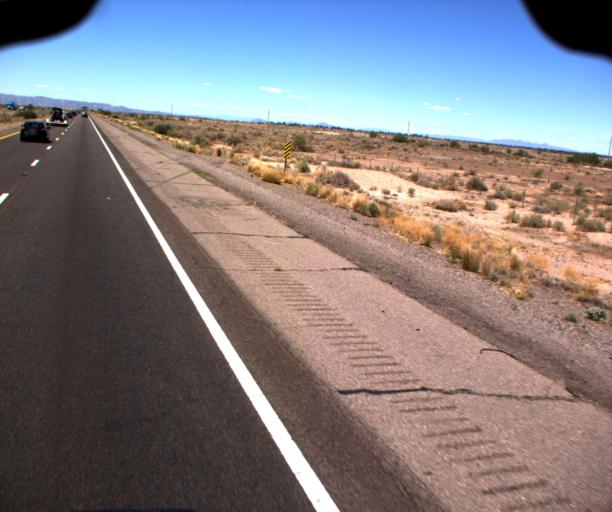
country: US
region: Arizona
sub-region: Pinal County
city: Casa Blanca
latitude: 33.1607
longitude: -111.8748
